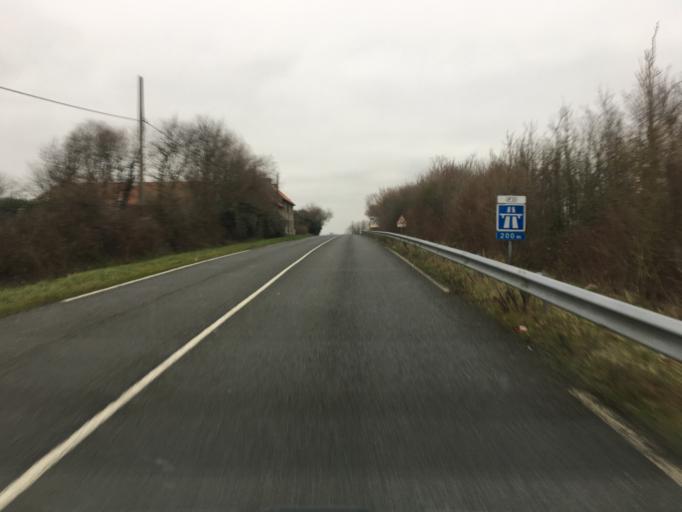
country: FR
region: Nord-Pas-de-Calais
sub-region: Departement du Pas-de-Calais
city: Wimille
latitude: 50.7697
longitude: 1.6460
